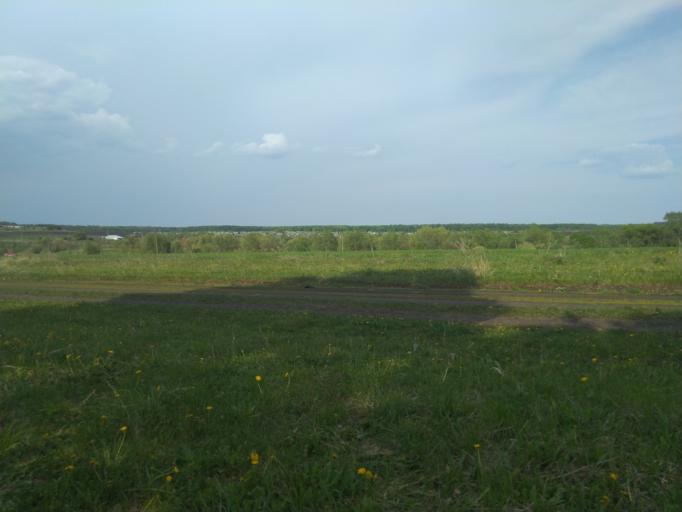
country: RU
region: Penza
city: Bogoslovka
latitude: 53.2059
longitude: 44.8259
